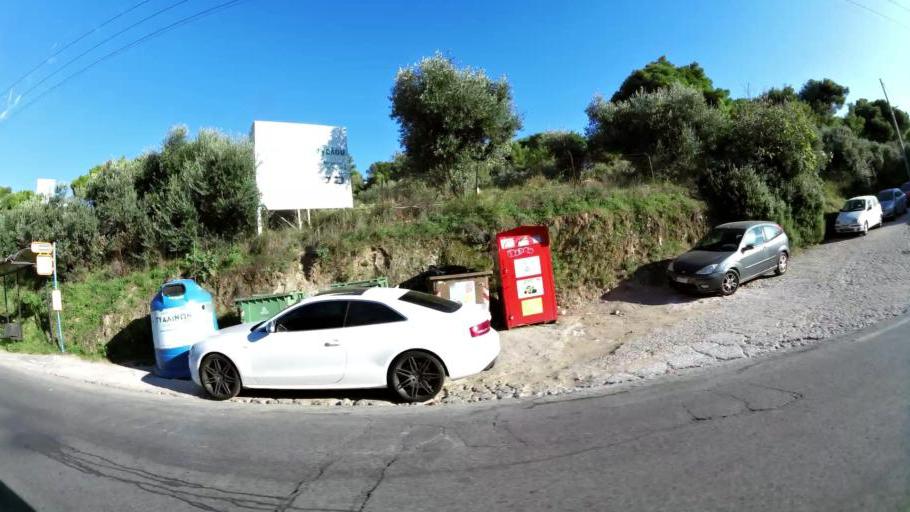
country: GR
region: Attica
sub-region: Nomarchia Athinas
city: Melissia
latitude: 38.0494
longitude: 23.8439
